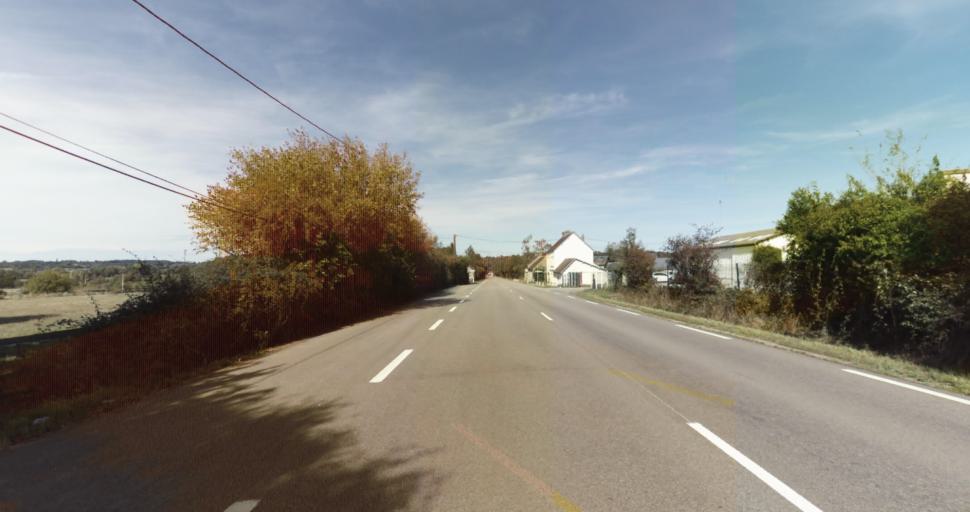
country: FR
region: Lower Normandy
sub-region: Departement de l'Orne
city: Gace
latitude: 48.7192
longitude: 0.2301
